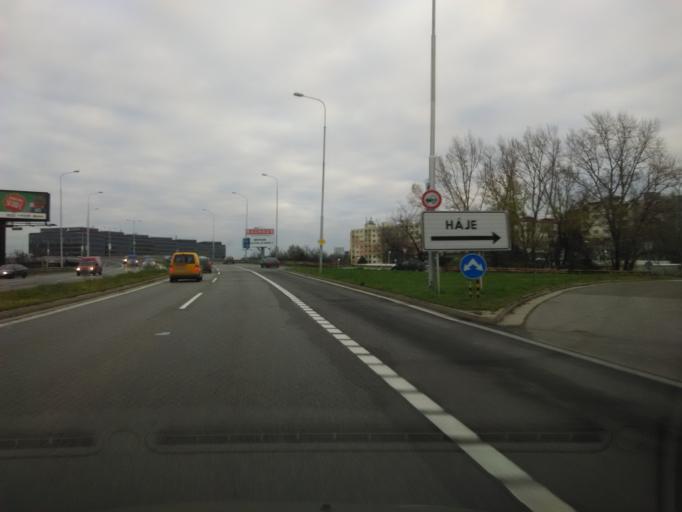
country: SK
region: Bratislavsky
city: Bratislava
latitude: 48.1248
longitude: 17.1040
